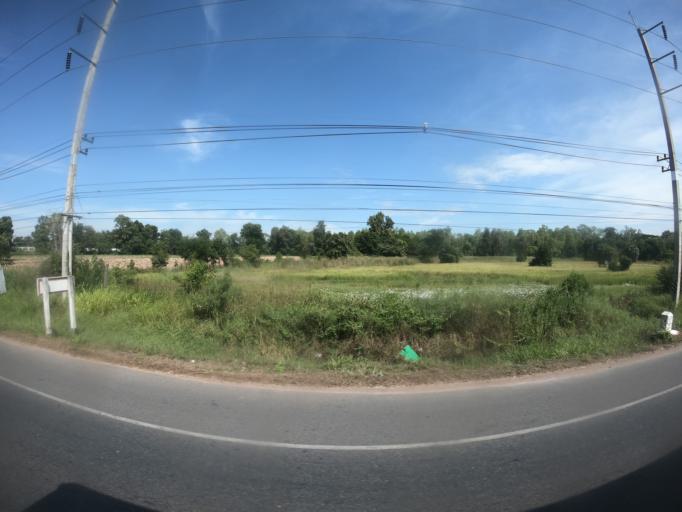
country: TH
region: Maha Sarakham
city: Chiang Yuen
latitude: 16.4417
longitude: 102.9736
